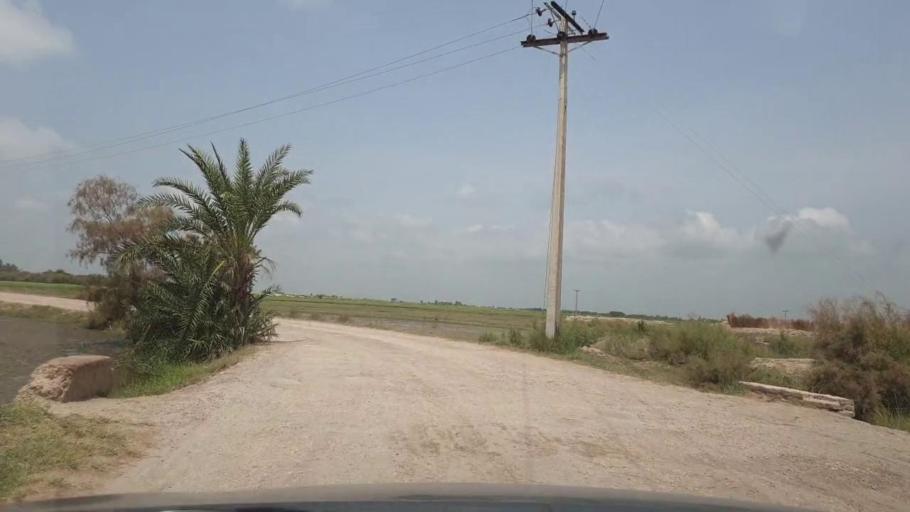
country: PK
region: Sindh
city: Ratodero
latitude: 27.9090
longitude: 68.3086
